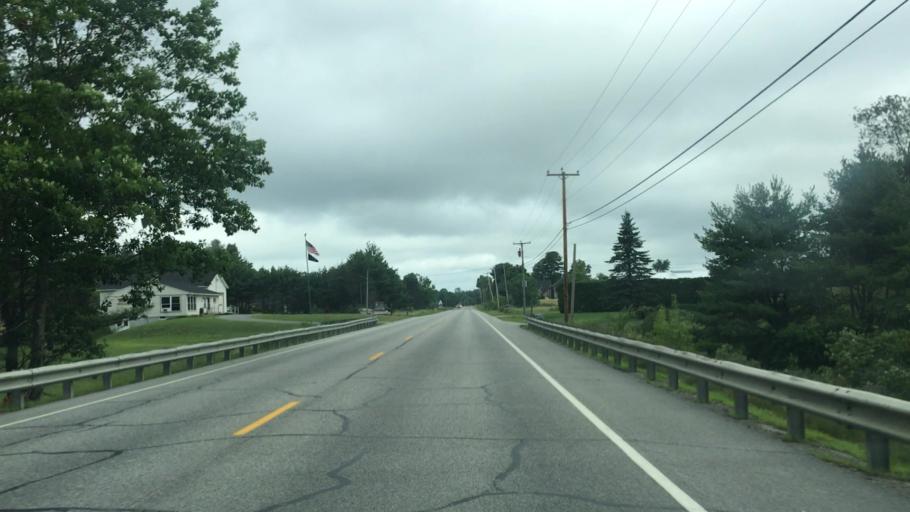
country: US
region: Maine
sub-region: Kennebec County
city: Pittston
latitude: 44.1505
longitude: -69.7438
